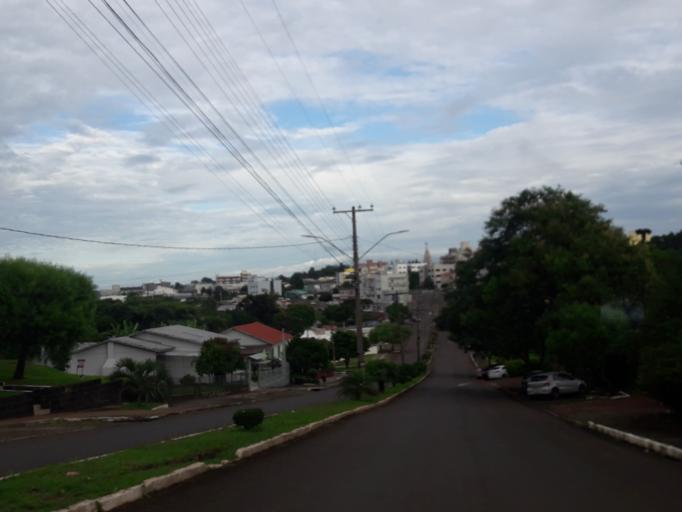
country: AR
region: Misiones
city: Bernardo de Irigoyen
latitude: -26.2583
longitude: -53.6341
